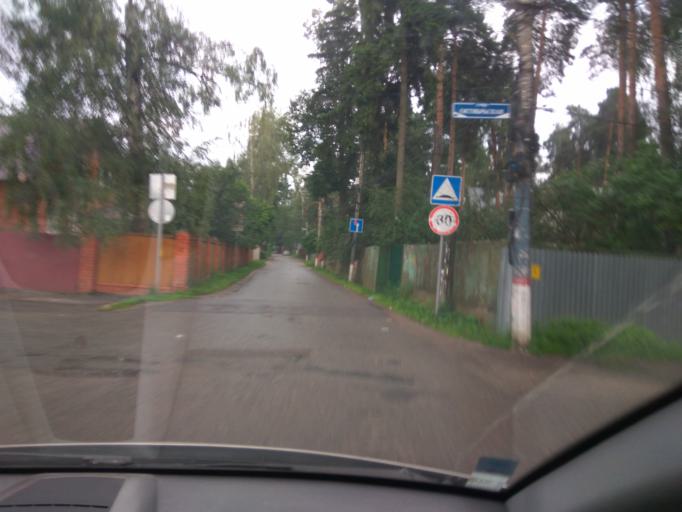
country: RU
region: Moskovskaya
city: Bykovo
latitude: 55.6284
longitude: 38.0759
